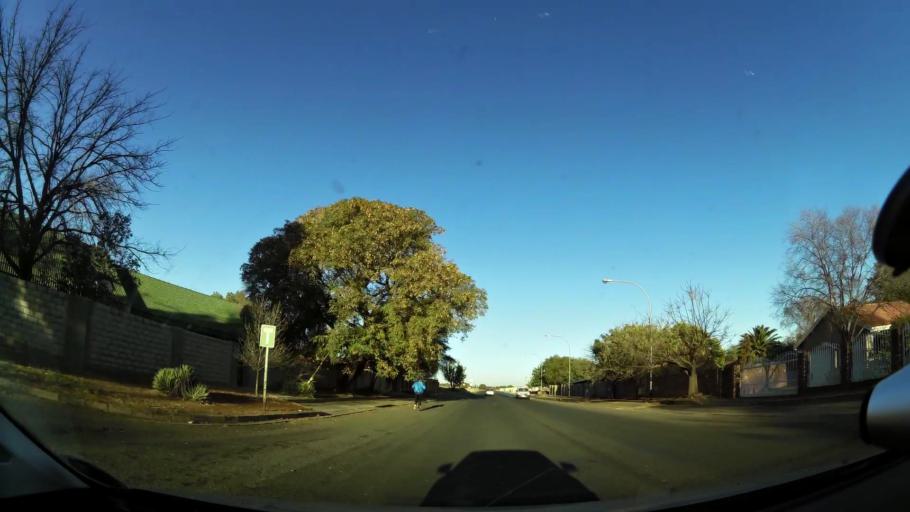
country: ZA
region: Northern Cape
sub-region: Frances Baard District Municipality
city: Kimberley
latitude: -28.7642
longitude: 24.7404
